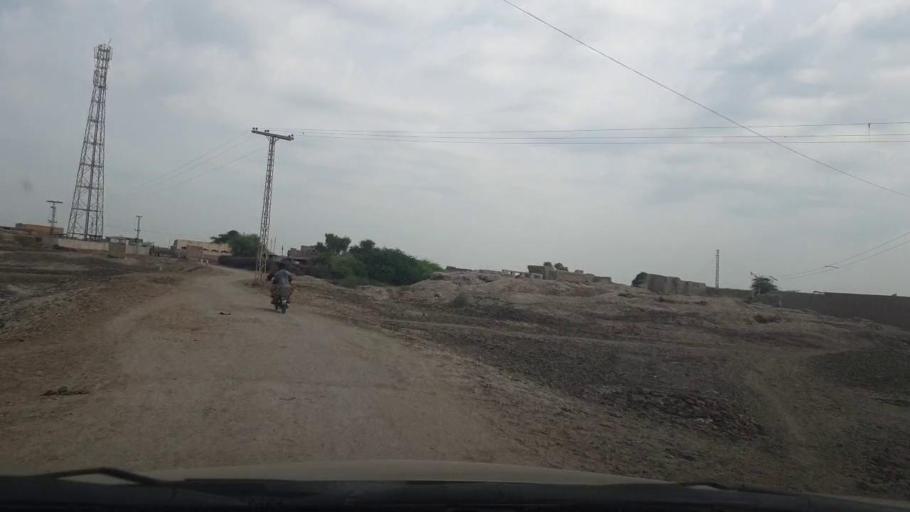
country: PK
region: Sindh
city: Ratodero
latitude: 27.7005
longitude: 68.2298
